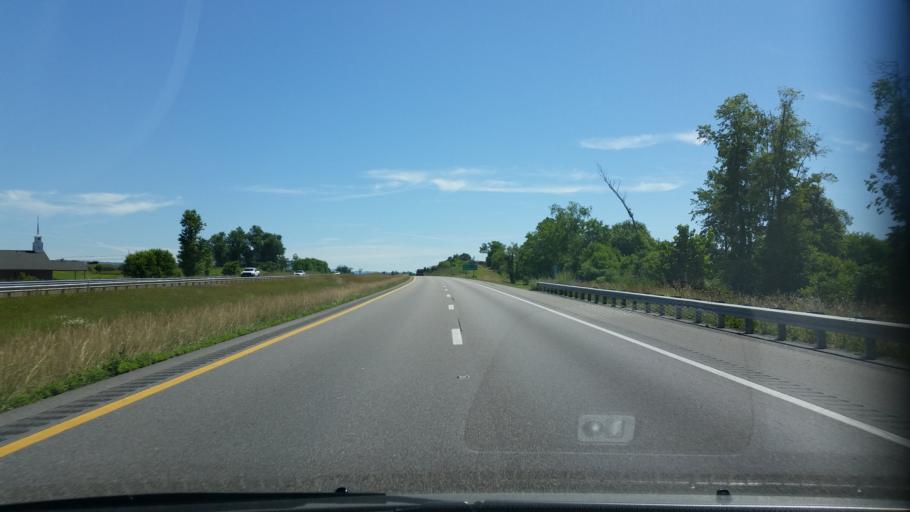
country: US
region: Virginia
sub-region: Washington County
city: Glade Spring
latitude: 36.7740
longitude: -81.7706
